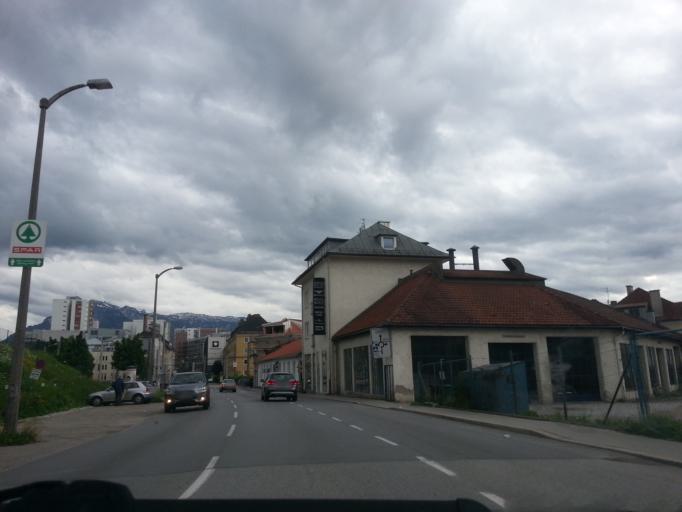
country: AT
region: Salzburg
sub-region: Salzburg Stadt
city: Salzburg
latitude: 47.8177
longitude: 13.0457
